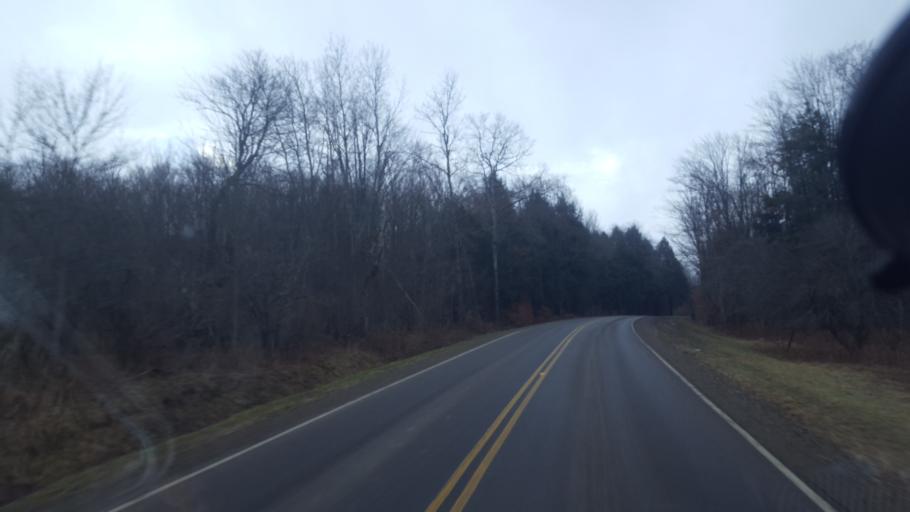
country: US
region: New York
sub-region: Allegany County
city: Andover
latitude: 42.0012
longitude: -77.7686
